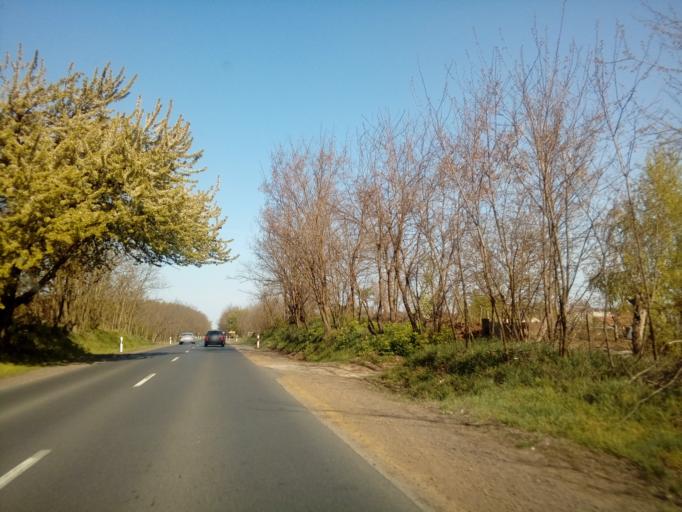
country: HU
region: Szabolcs-Szatmar-Bereg
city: Nagykallo
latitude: 47.9008
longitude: 21.7911
